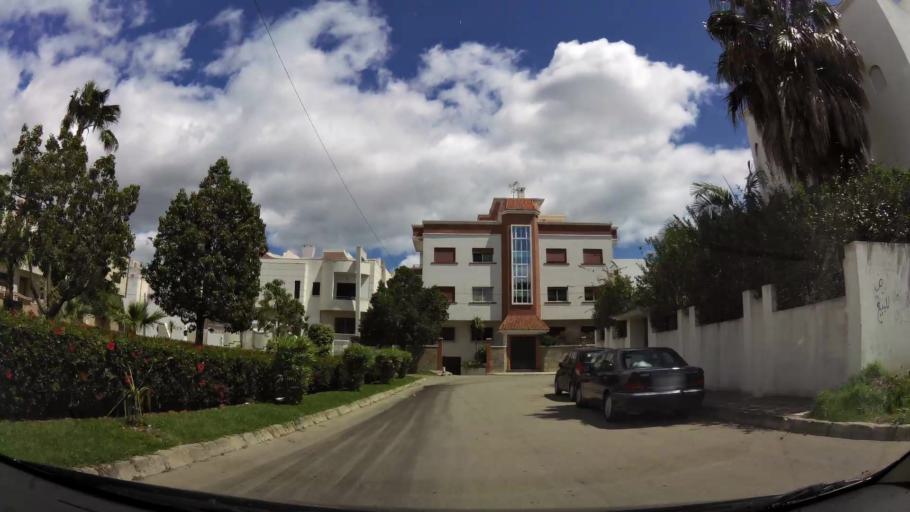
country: MA
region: Tanger-Tetouan
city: Tetouan
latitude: 35.5744
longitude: -5.3436
